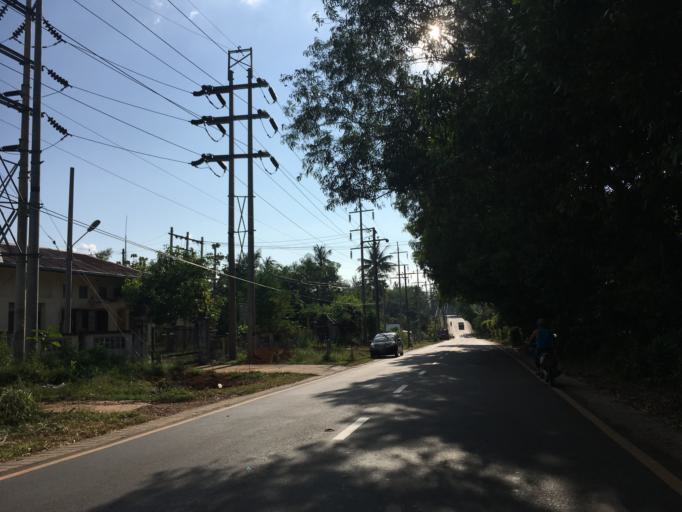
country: MM
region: Mon
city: Mawlamyine
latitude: 16.4350
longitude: 97.6519
